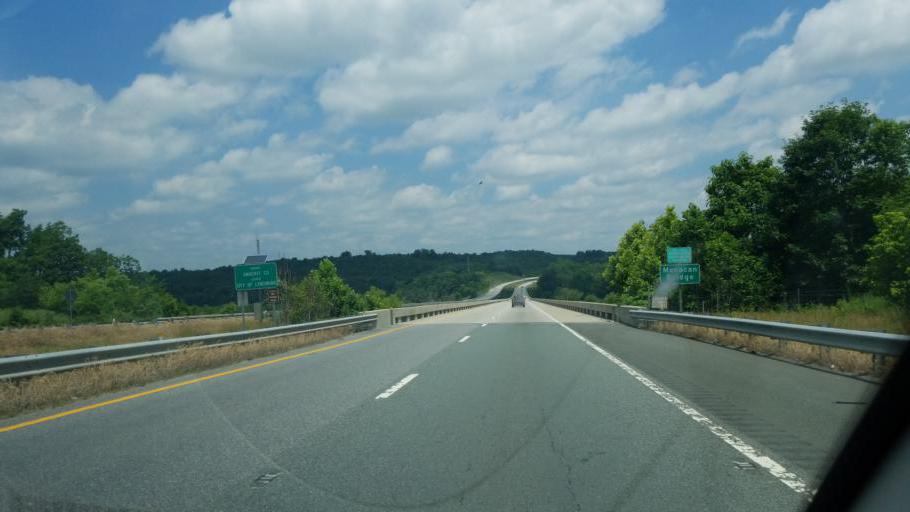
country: US
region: Virginia
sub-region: Amherst County
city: Madison Heights
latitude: 37.3942
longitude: -79.0887
